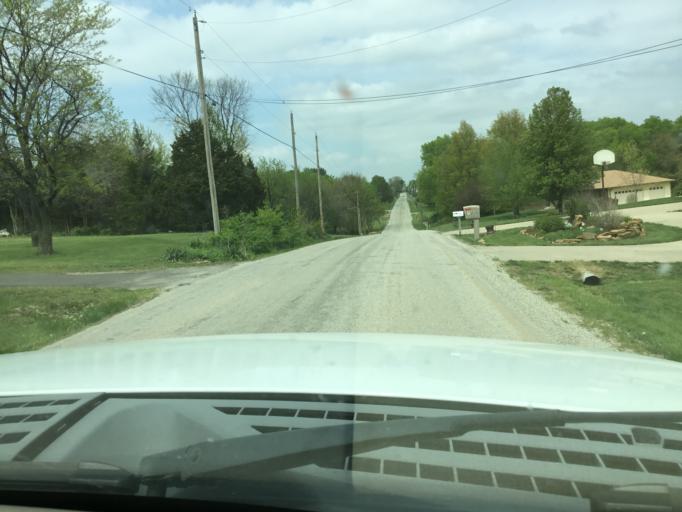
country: US
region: Kansas
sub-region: Shawnee County
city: Topeka
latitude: 38.9739
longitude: -95.5863
